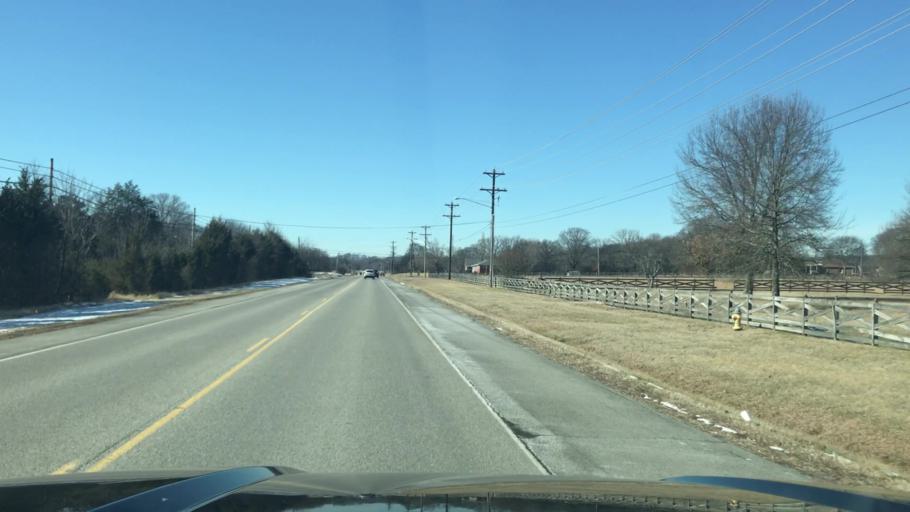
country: US
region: Tennessee
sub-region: Wilson County
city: Lebanon
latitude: 36.1947
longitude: -86.3390
